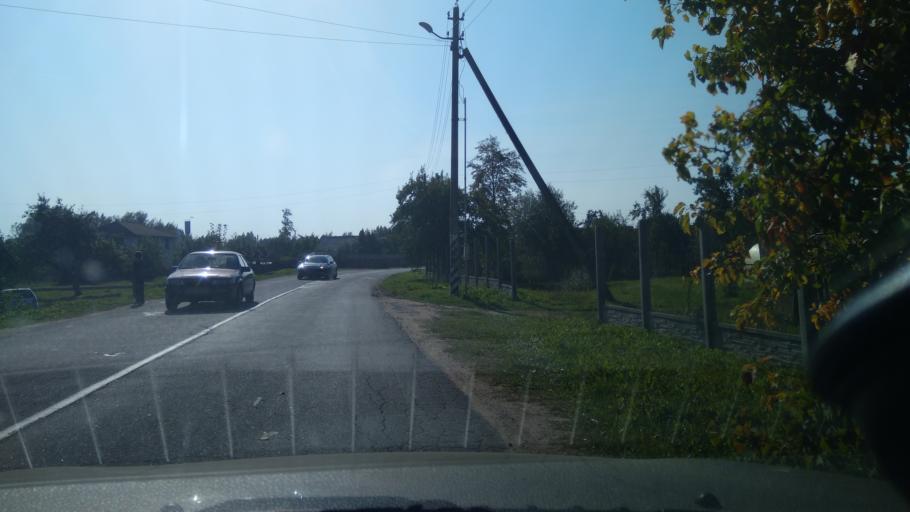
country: BY
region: Minsk
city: Rakaw
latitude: 54.0120
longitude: 27.0512
